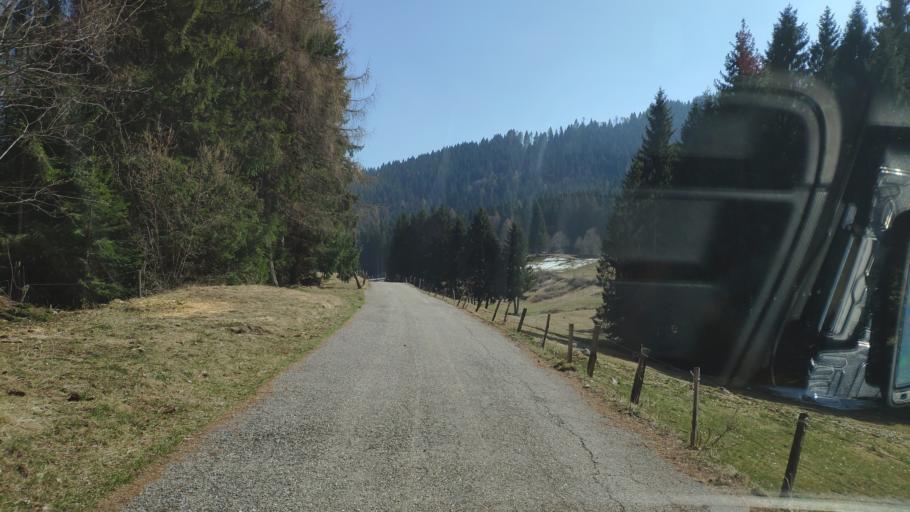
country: IT
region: Veneto
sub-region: Provincia di Vicenza
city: Enego
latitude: 45.9610
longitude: 11.6753
